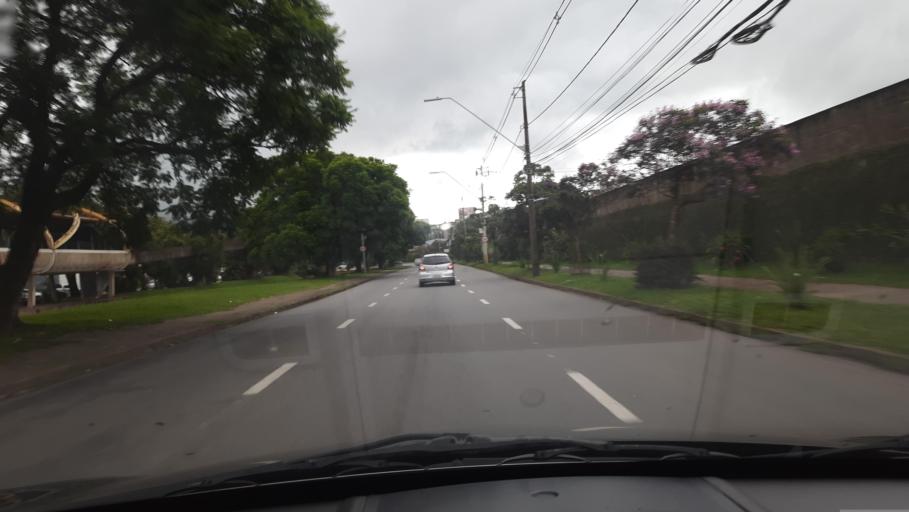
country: BR
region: Minas Gerais
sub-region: Pocos De Caldas
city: Pocos de Caldas
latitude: -21.7830
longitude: -46.5976
